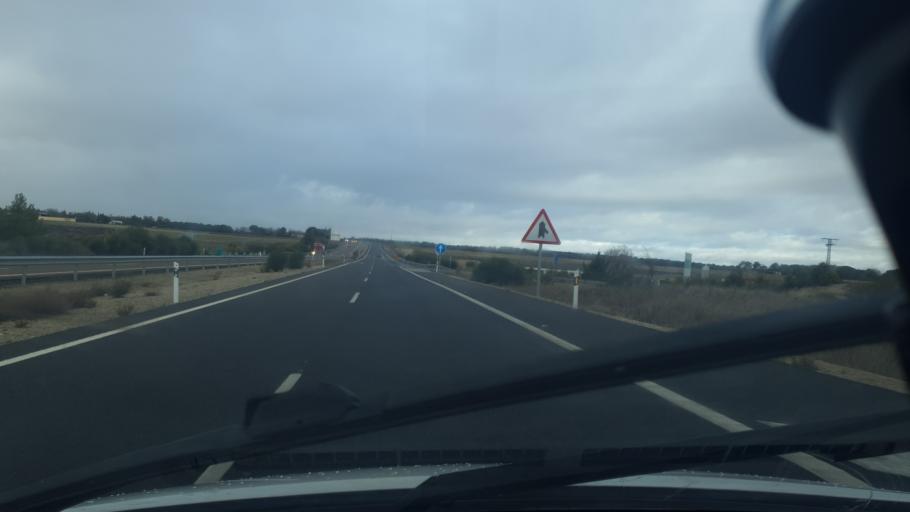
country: ES
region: Castille and Leon
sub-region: Provincia de Segovia
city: Cuellar
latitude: 41.4057
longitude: -4.2950
